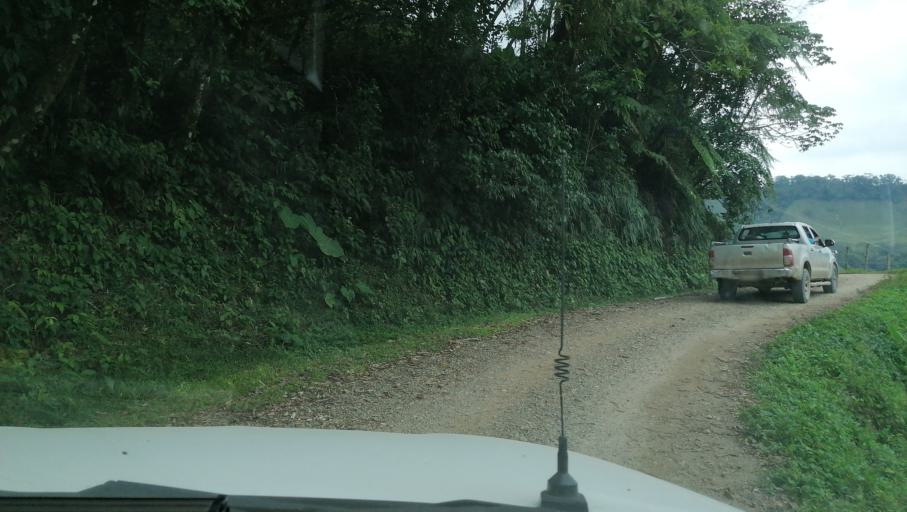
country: MX
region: Chiapas
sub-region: Francisco Leon
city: San Miguel la Sardina
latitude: 17.3321
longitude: -93.3102
